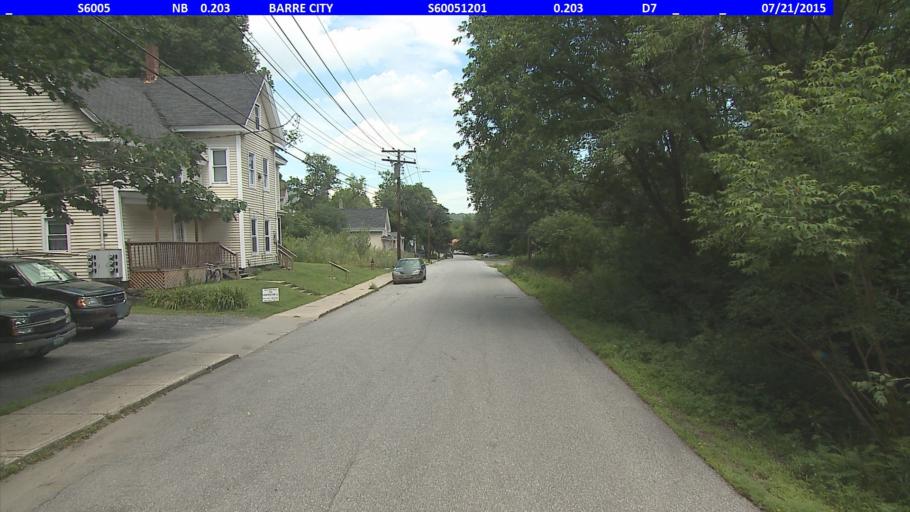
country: US
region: Vermont
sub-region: Washington County
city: Barre
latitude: 44.1935
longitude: -72.5020
